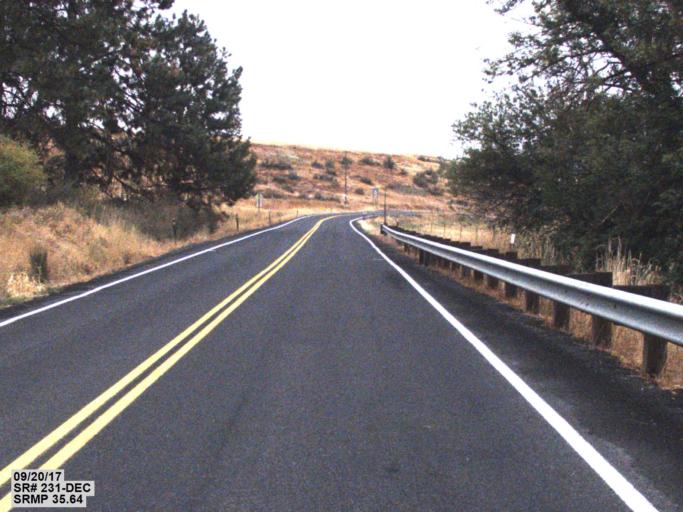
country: US
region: Washington
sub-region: Spokane County
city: Medical Lake
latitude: 47.7335
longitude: -117.8722
